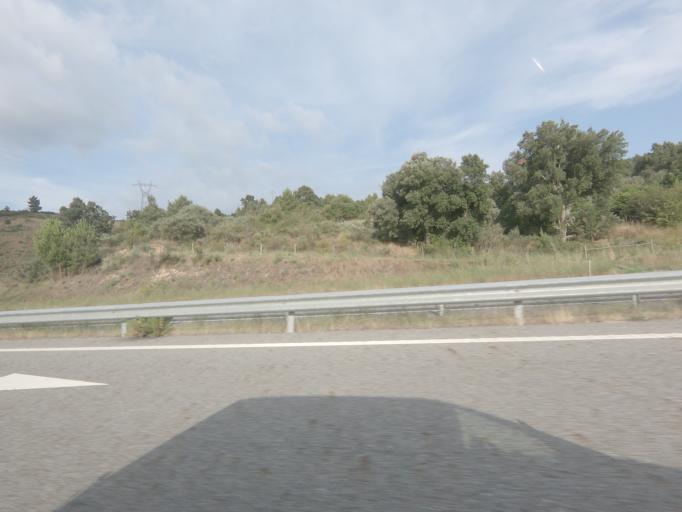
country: PT
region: Vila Real
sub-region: Boticas
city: Boticas
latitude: 41.6724
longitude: -7.5682
